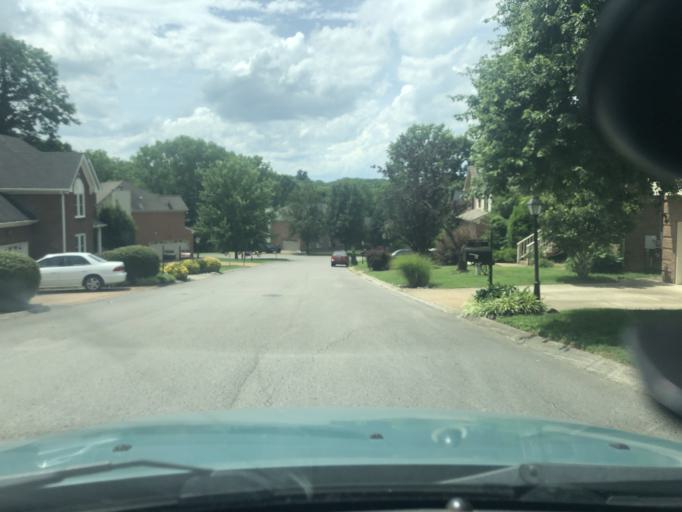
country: US
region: Tennessee
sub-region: Davidson County
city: Lakewood
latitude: 36.1313
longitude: -86.6355
